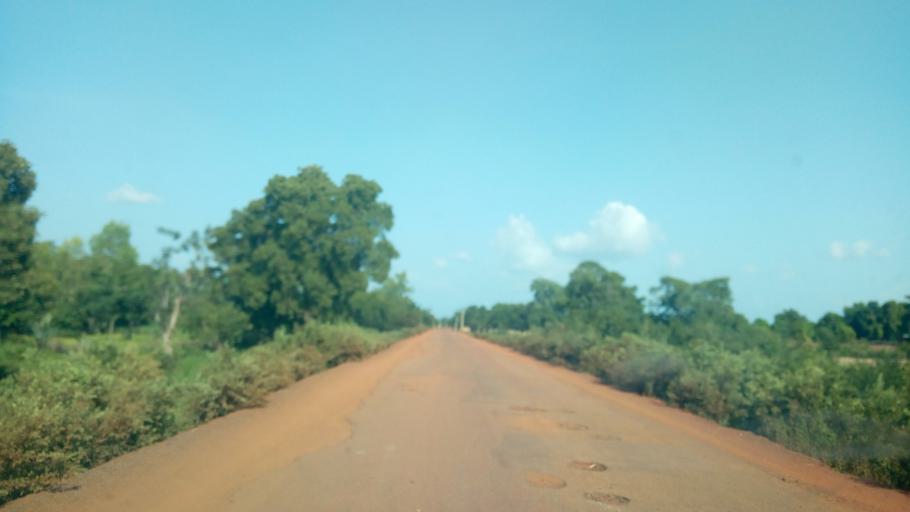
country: ML
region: Sikasso
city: Yorosso
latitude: 12.1849
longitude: -4.8182
